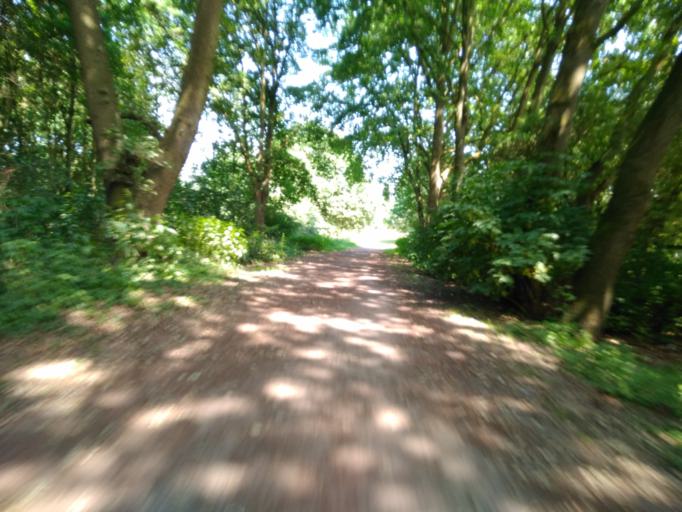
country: DE
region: North Rhine-Westphalia
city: Dorsten
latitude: 51.6495
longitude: 6.9480
